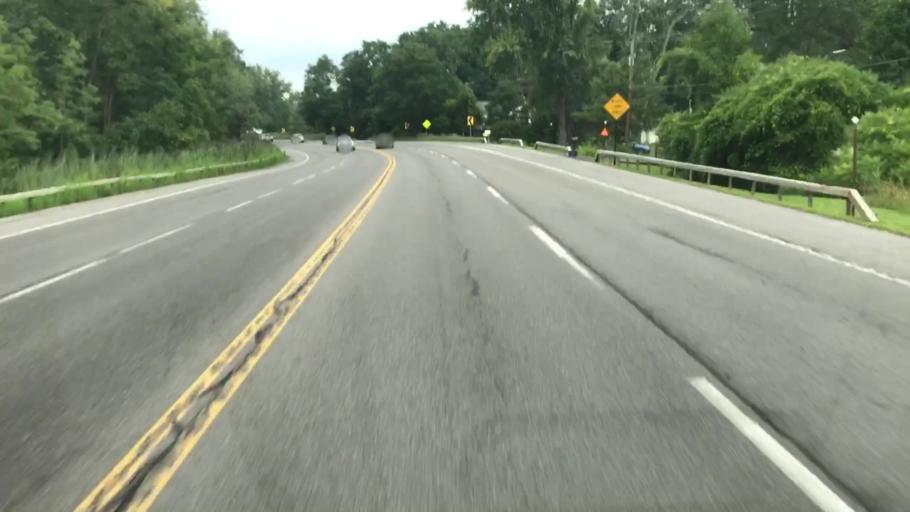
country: US
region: New York
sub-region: Onondaga County
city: Liverpool
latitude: 43.1738
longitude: -76.2094
